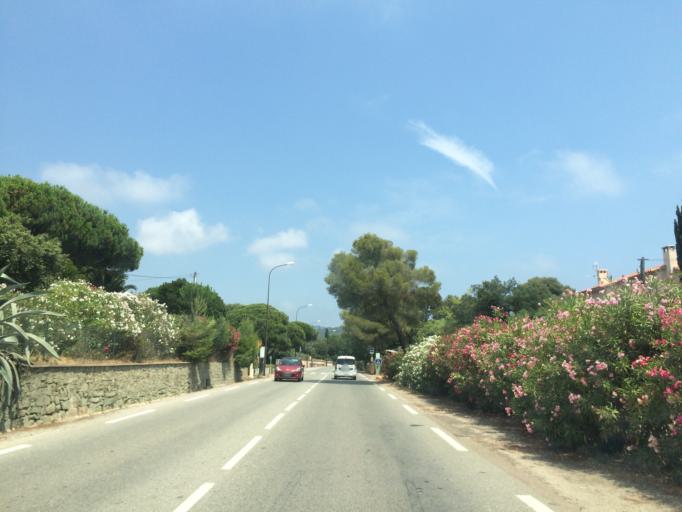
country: FR
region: Provence-Alpes-Cote d'Azur
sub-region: Departement du Var
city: Sainte-Maxime
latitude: 43.3369
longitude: 6.6730
